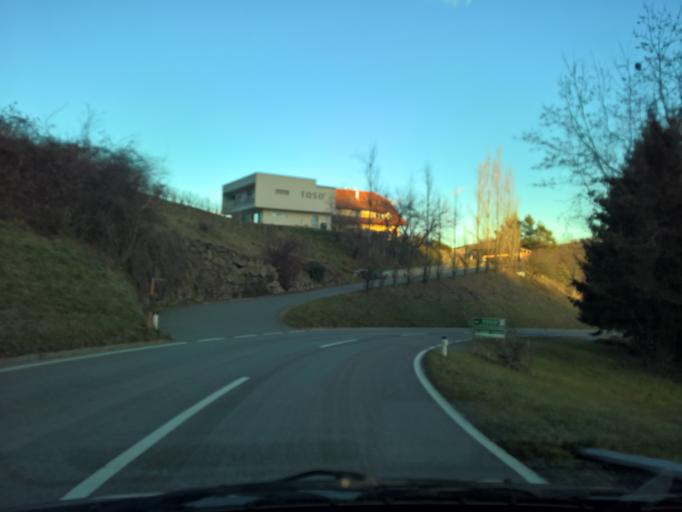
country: AT
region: Styria
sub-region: Politischer Bezirk Leibnitz
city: Leutschach
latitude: 46.6854
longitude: 15.4843
